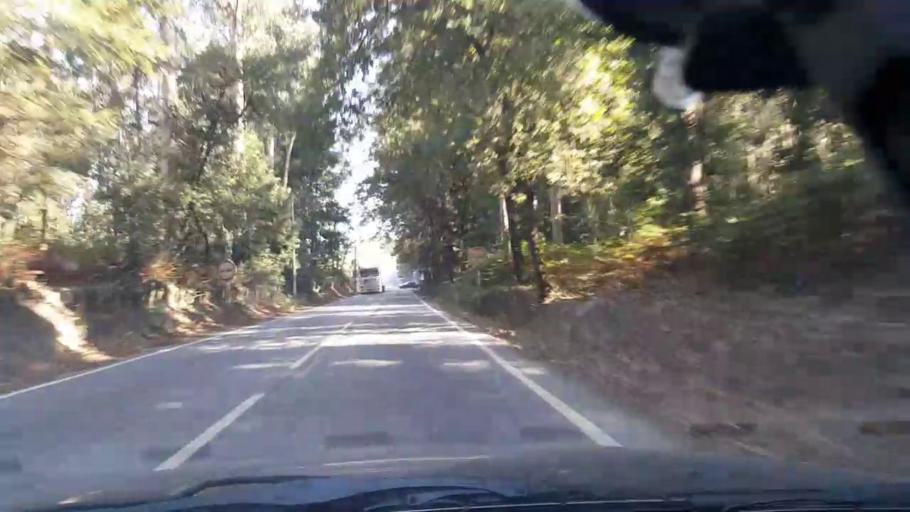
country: PT
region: Porto
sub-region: Vila do Conde
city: Arvore
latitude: 41.3620
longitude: -8.6745
